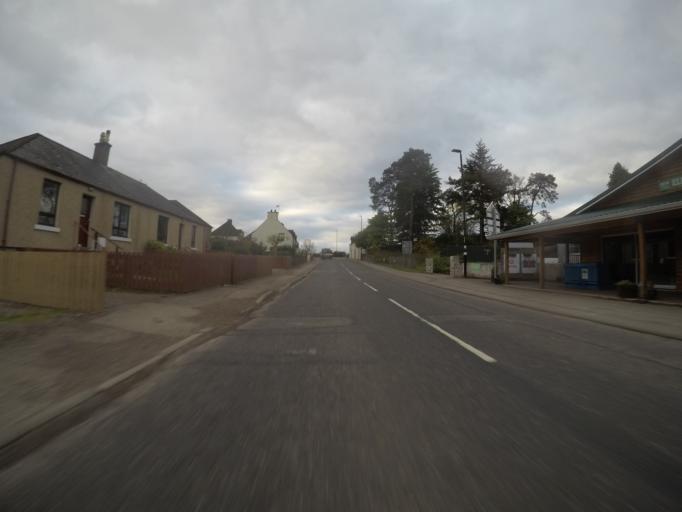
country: GB
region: Scotland
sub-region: Highland
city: Spean Bridge
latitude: 57.1419
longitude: -4.6863
